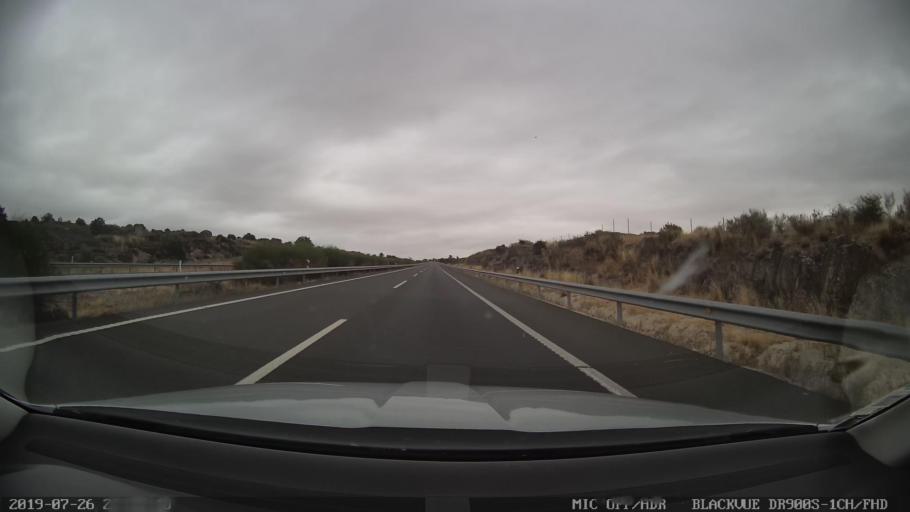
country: ES
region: Extremadura
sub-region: Provincia de Caceres
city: Trujillo
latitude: 39.4356
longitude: -5.8771
